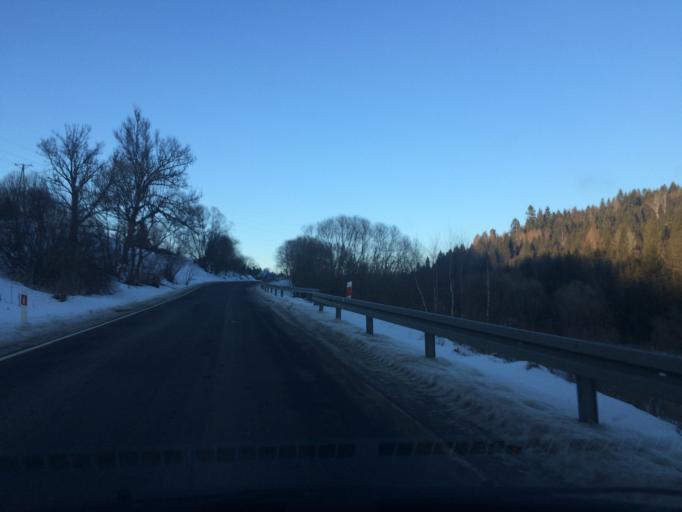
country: PL
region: Subcarpathian Voivodeship
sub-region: Powiat bieszczadzki
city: Lutowiska
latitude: 49.2186
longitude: 22.6933
